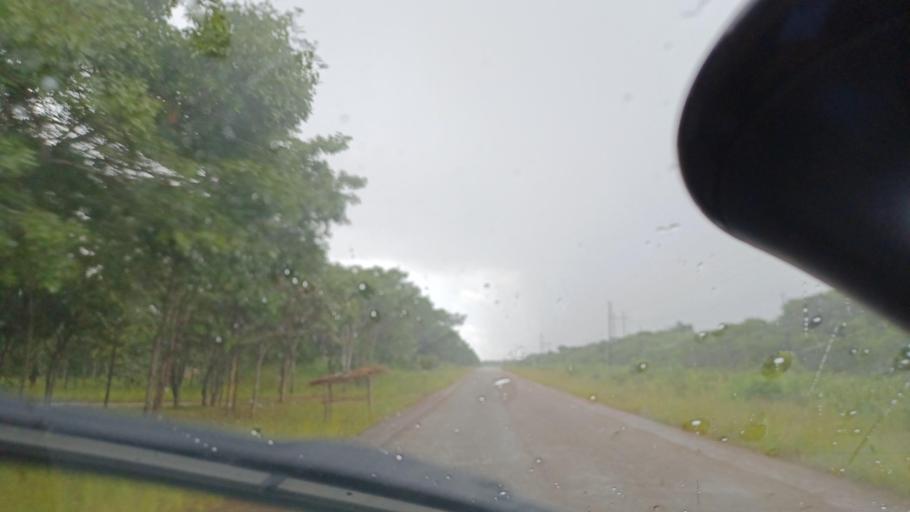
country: ZM
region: North-Western
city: Kasempa
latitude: -13.0913
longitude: 25.9350
